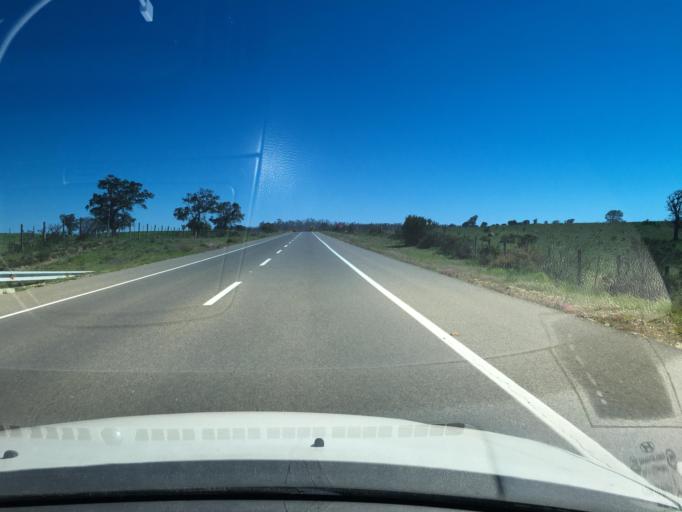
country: CL
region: Valparaiso
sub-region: San Antonio Province
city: El Tabo
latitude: -33.4067
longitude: -71.5405
